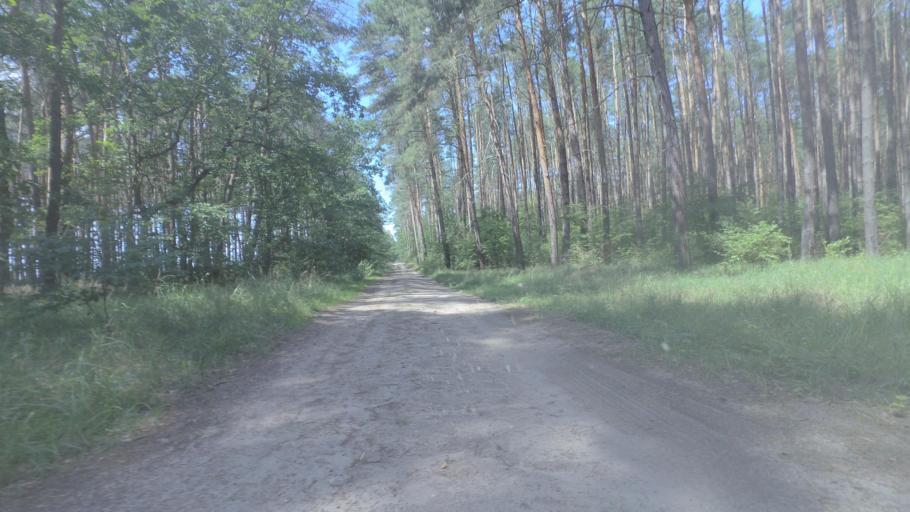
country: DE
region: Brandenburg
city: Am Mellensee
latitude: 52.2309
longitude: 13.3888
